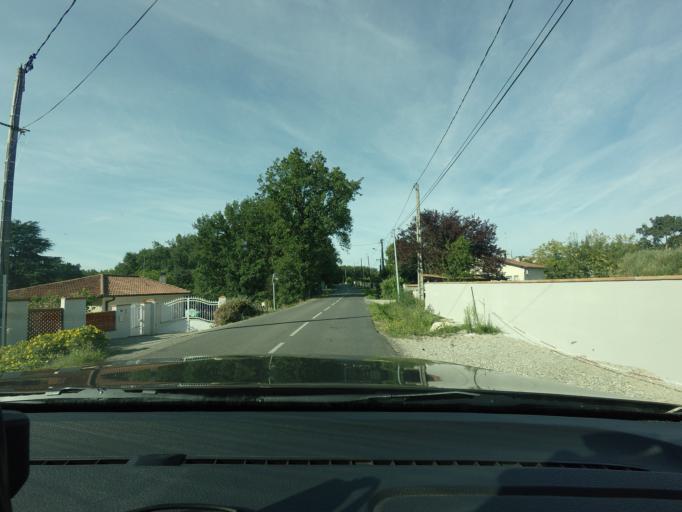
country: FR
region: Midi-Pyrenees
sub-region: Departement de la Haute-Garonne
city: Cornebarrieu
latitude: 43.6408
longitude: 1.3165
